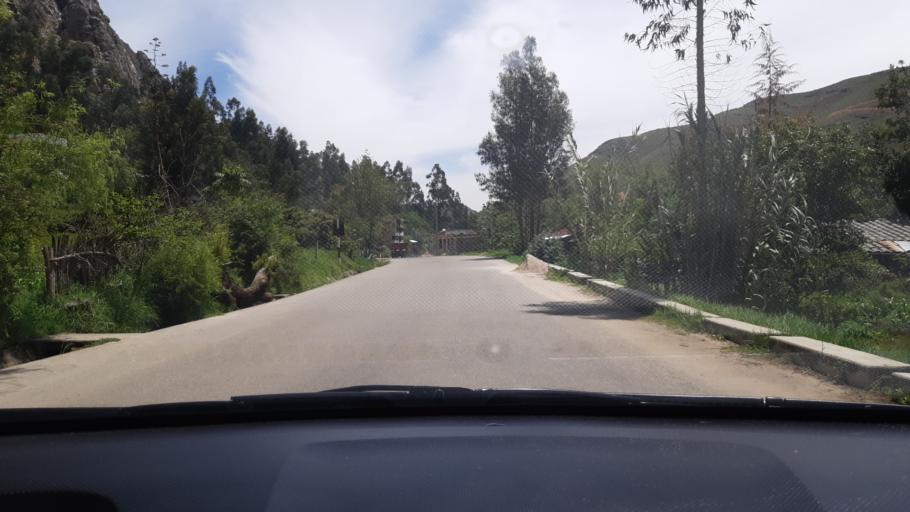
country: PE
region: Cajamarca
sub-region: Provincia de Cajamarca
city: Llacanora
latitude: -7.1832
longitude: -78.4455
